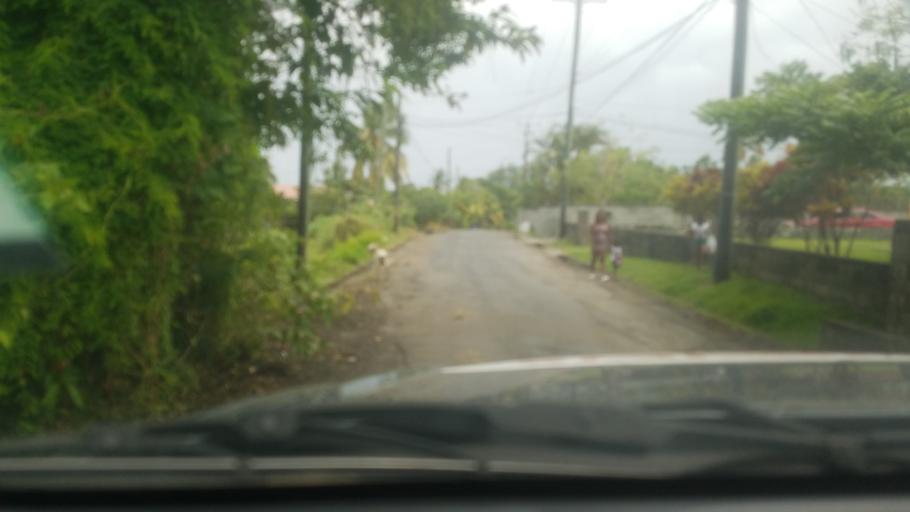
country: LC
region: Laborie Quarter
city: Laborie
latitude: 13.7688
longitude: -60.9778
